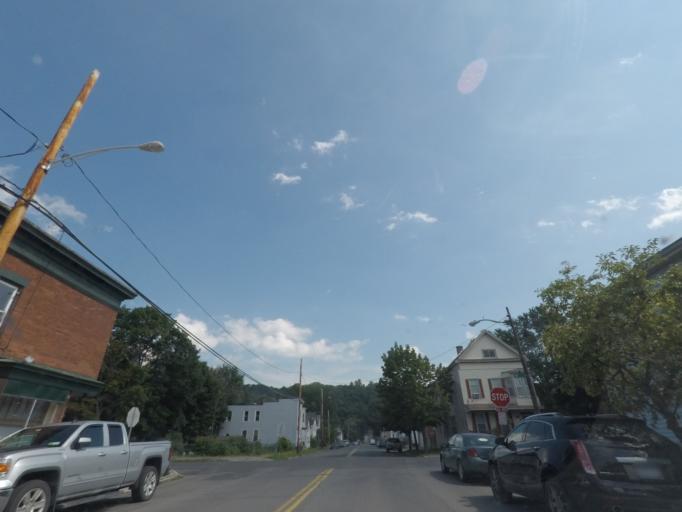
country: US
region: New York
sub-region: Saratoga County
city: Waterford
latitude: 42.7699
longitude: -73.6745
